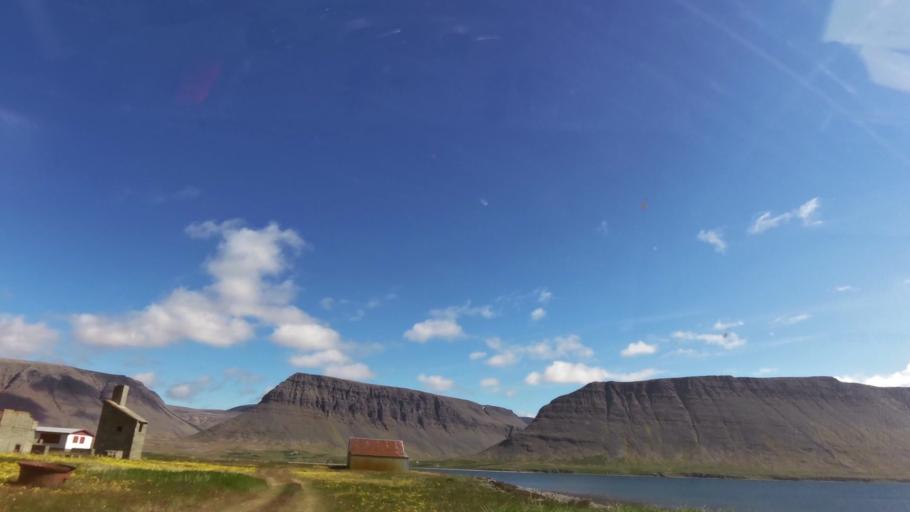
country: IS
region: West
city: Olafsvik
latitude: 65.6393
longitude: -23.9315
